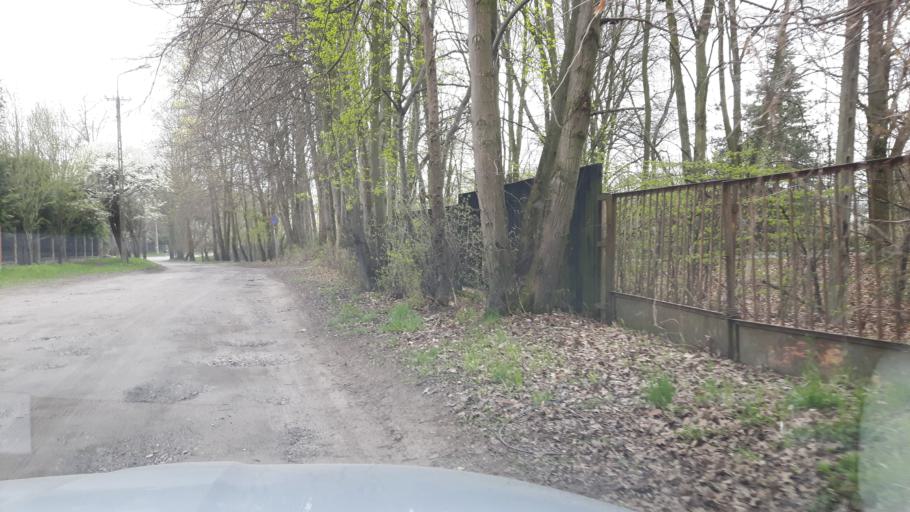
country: PL
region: Masovian Voivodeship
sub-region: Powiat wolominski
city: Kobylka
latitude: 52.3423
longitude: 21.1947
